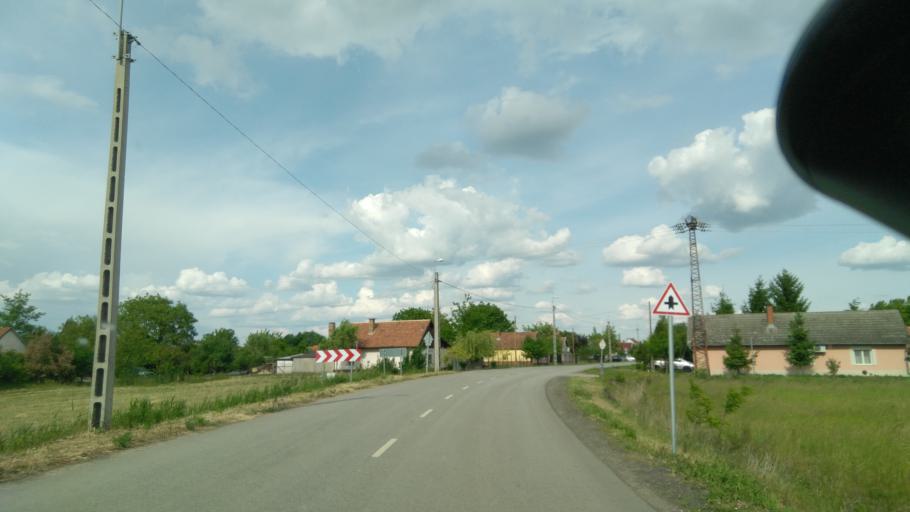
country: HU
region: Bekes
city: Battonya
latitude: 46.2914
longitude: 21.0016
